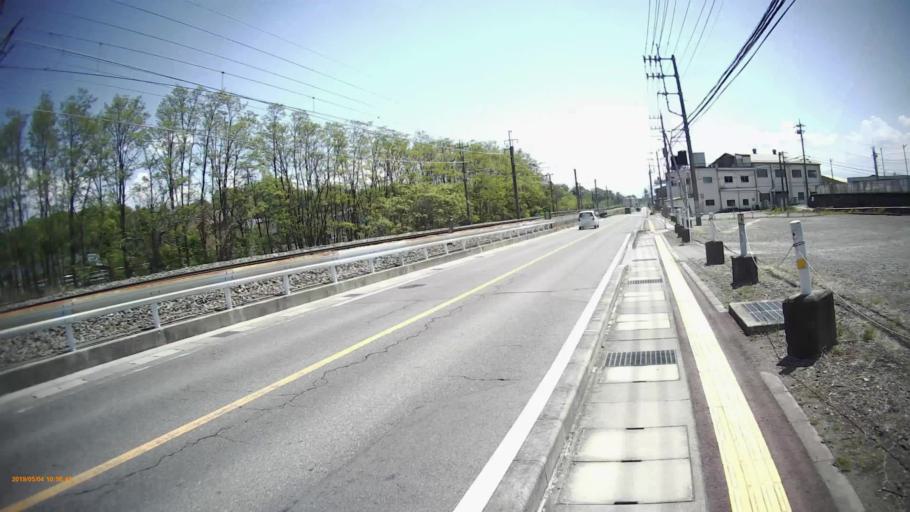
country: JP
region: Yamanashi
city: Nirasaki
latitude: 35.7006
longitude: 138.4611
